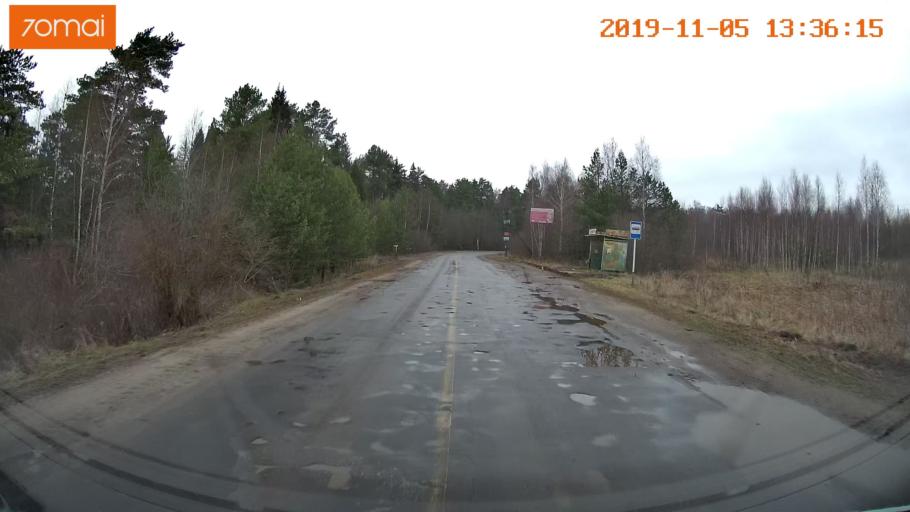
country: RU
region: Ivanovo
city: Shuya
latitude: 56.9133
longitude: 41.3831
